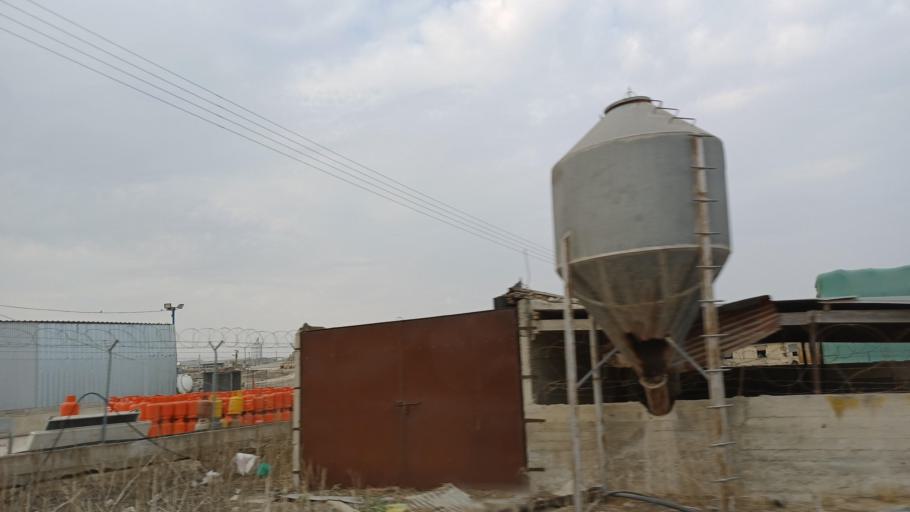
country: CY
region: Larnaka
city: Athienou
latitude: 35.0403
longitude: 33.5565
